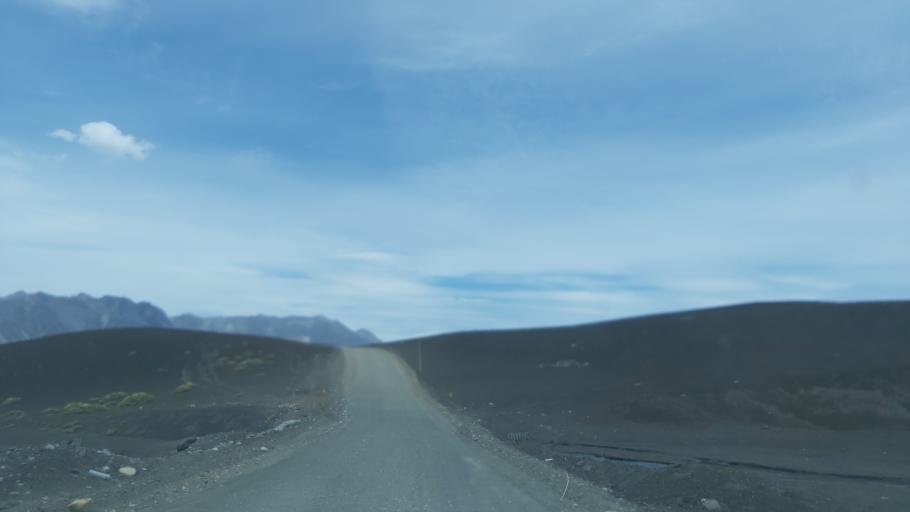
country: AR
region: Neuquen
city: Andacollo
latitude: -37.4129
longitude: -71.2918
